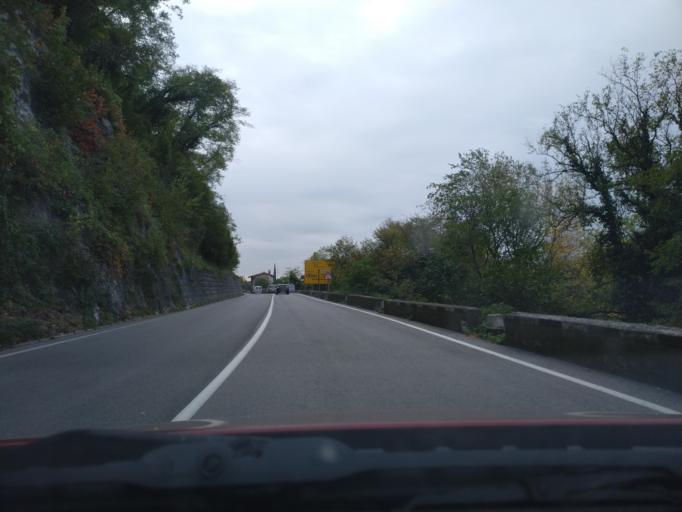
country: SI
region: Nova Gorica
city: Solkan
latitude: 45.9782
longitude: 13.6528
